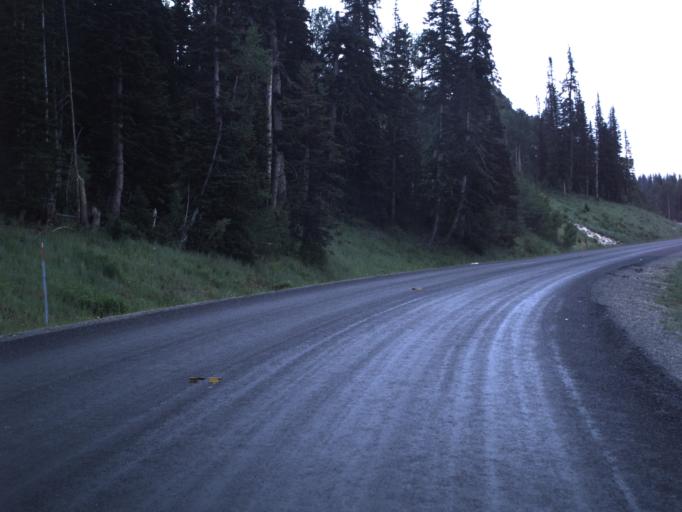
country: US
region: Utah
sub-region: Summit County
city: Francis
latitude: 40.4960
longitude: -111.0349
